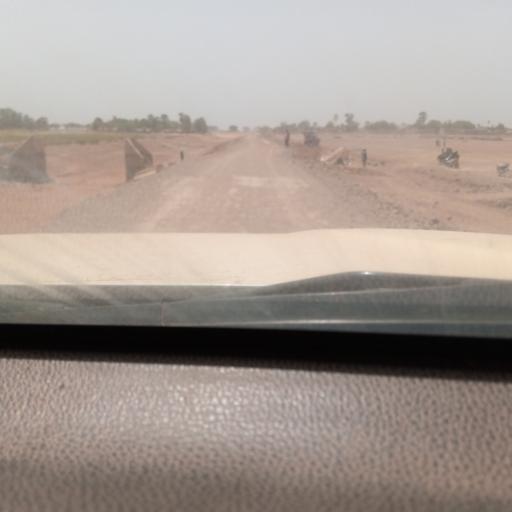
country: ML
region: Mopti
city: Tenenkou
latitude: 14.4316
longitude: -4.8789
